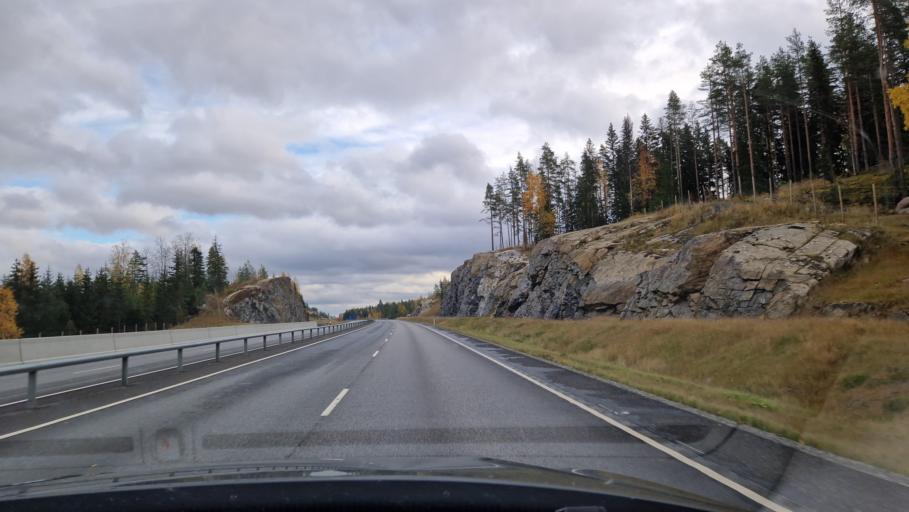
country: FI
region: Southern Savonia
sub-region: Mikkeli
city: Mikkeli
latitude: 61.7464
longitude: 27.4957
